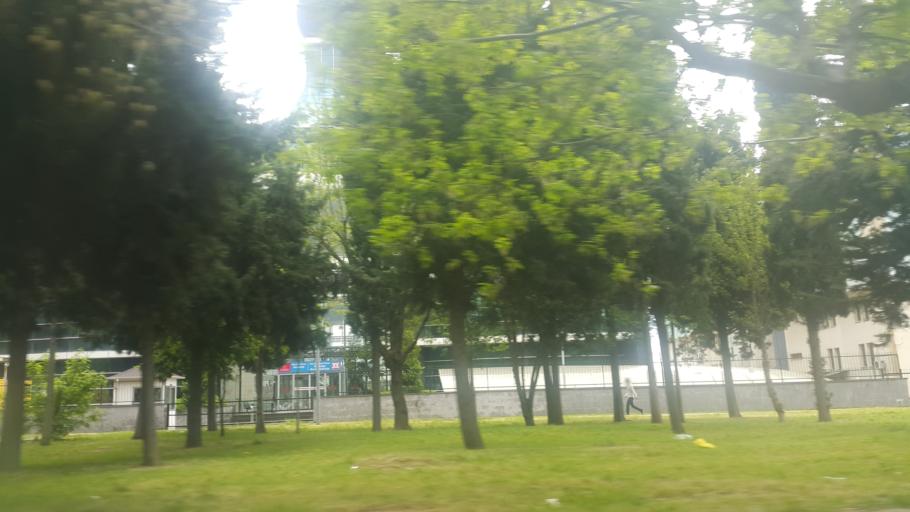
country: TR
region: Mersin
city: Mercin
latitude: 36.8014
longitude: 34.6367
